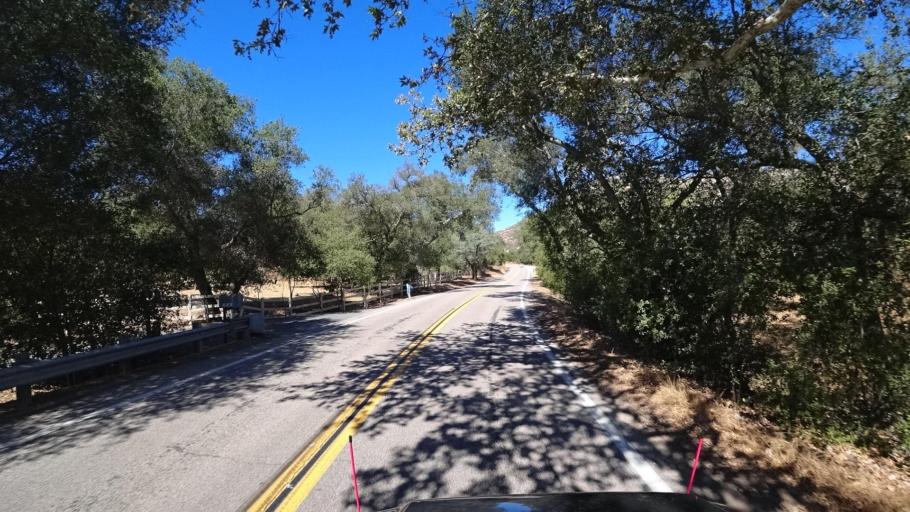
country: US
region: California
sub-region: San Diego County
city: Alpine
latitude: 32.7073
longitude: -116.7371
